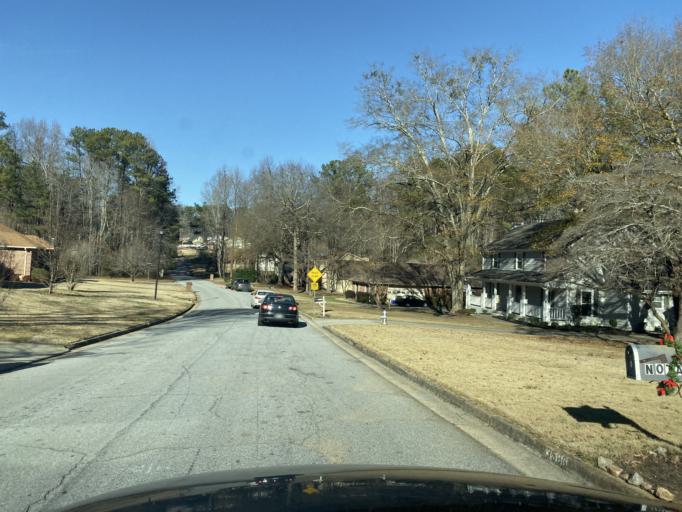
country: US
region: Georgia
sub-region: DeKalb County
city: Pine Mountain
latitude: 33.6767
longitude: -84.1572
